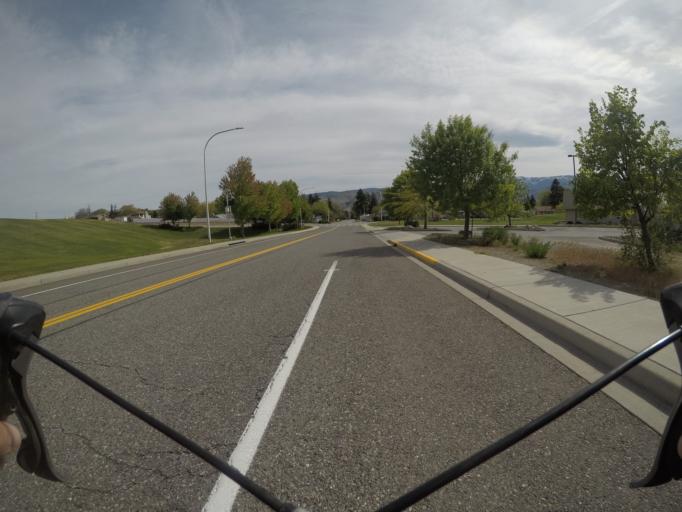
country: US
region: Washington
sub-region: Douglas County
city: East Wenatchee Bench
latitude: 47.4178
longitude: -120.2766
